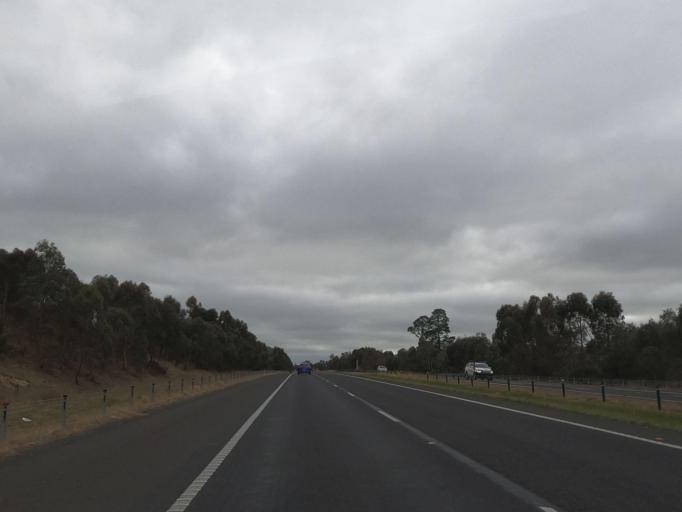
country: AU
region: Victoria
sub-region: Mount Alexander
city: Castlemaine
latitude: -36.9841
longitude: 144.2532
